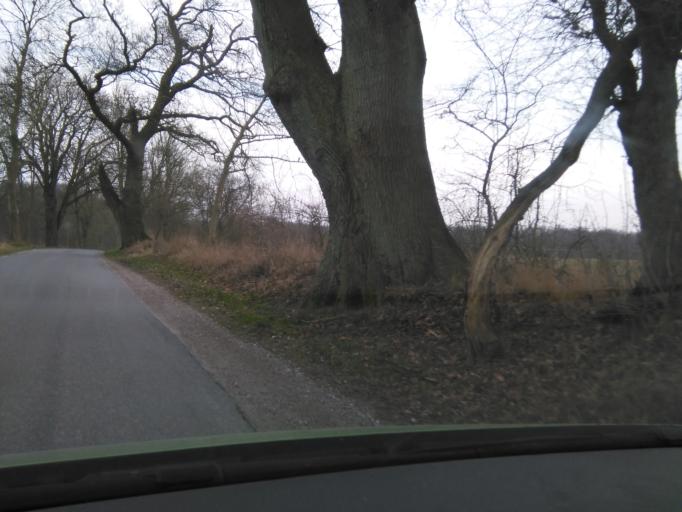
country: DK
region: Central Jutland
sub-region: Arhus Kommune
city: Beder
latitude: 56.0846
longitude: 10.2282
